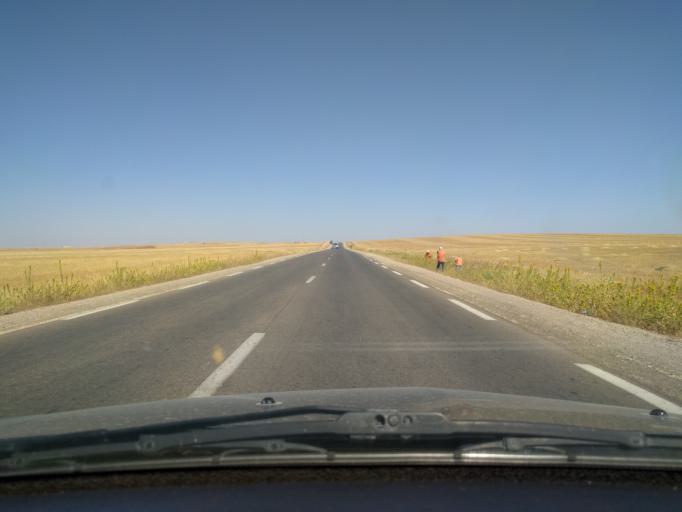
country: DZ
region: Tiaret
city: Frenda
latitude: 34.8820
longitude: 1.1925
